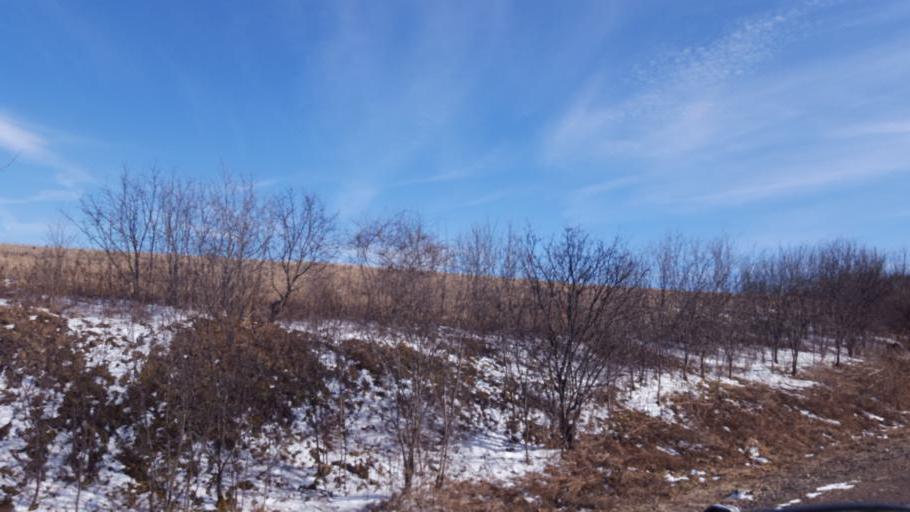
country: US
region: New York
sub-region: Allegany County
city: Wellsville
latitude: 42.1183
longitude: -77.9954
